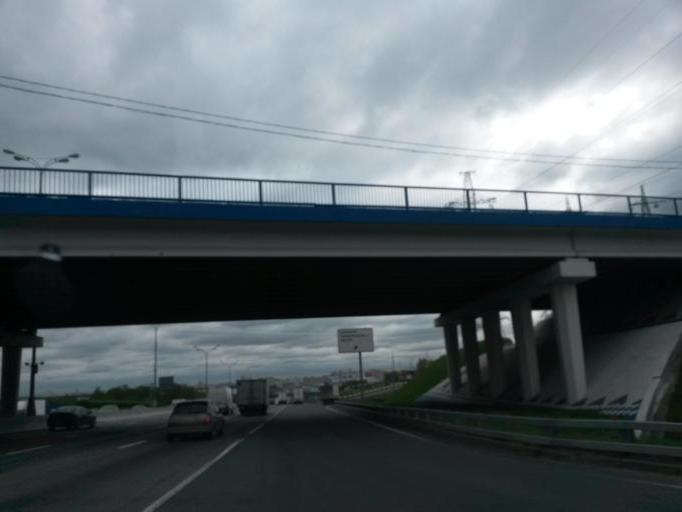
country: RU
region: Moskovskaya
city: Alekseyevka
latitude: 55.6403
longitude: 37.8197
